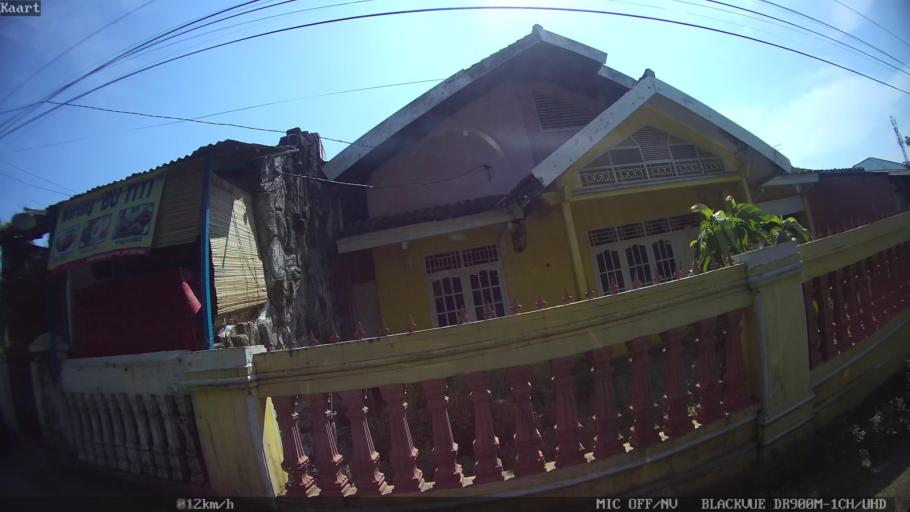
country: ID
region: Lampung
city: Kedaton
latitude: -5.3719
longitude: 105.2505
